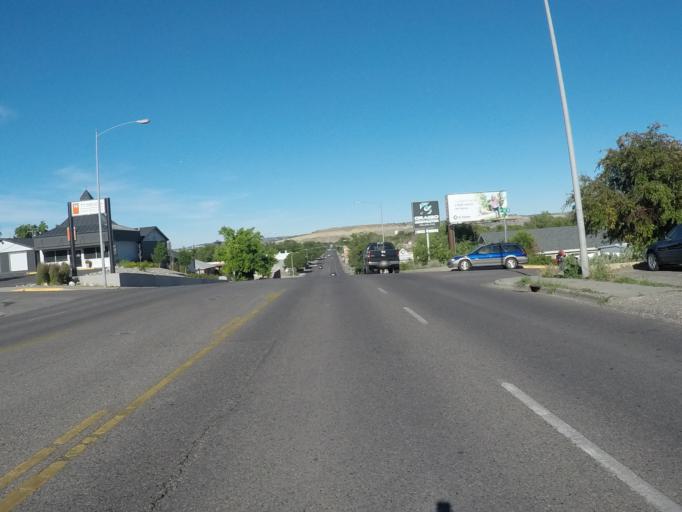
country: US
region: Montana
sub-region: Yellowstone County
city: Billings
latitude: 45.7770
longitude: -108.5438
